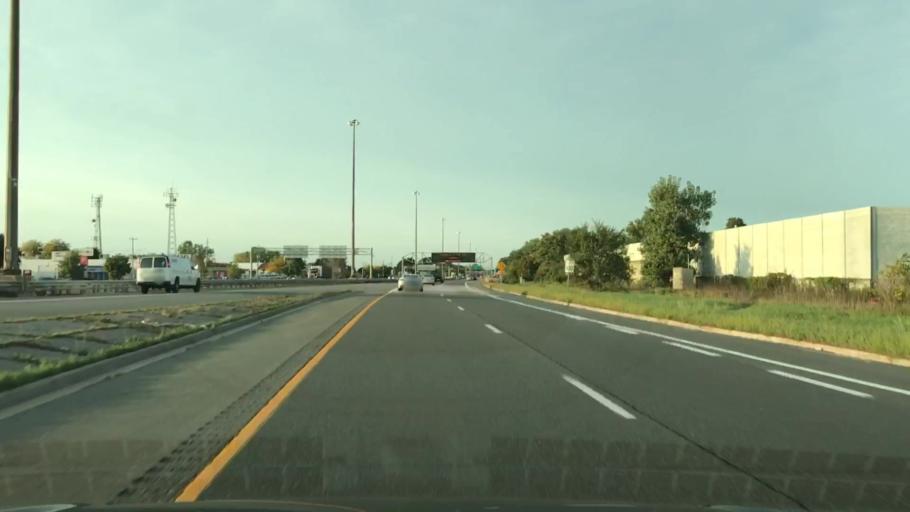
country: CA
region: Ontario
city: Niagara Falls
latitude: 43.1040
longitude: -79.1193
